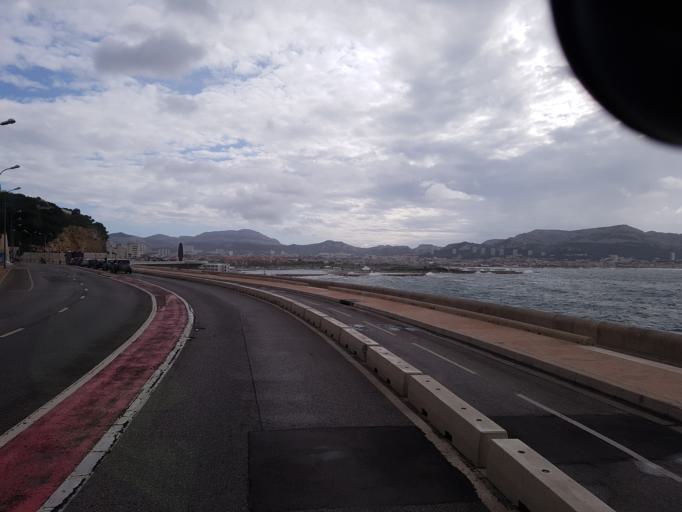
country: FR
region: Provence-Alpes-Cote d'Azur
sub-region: Departement des Bouches-du-Rhone
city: Marseille 07
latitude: 43.2705
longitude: 5.3634
